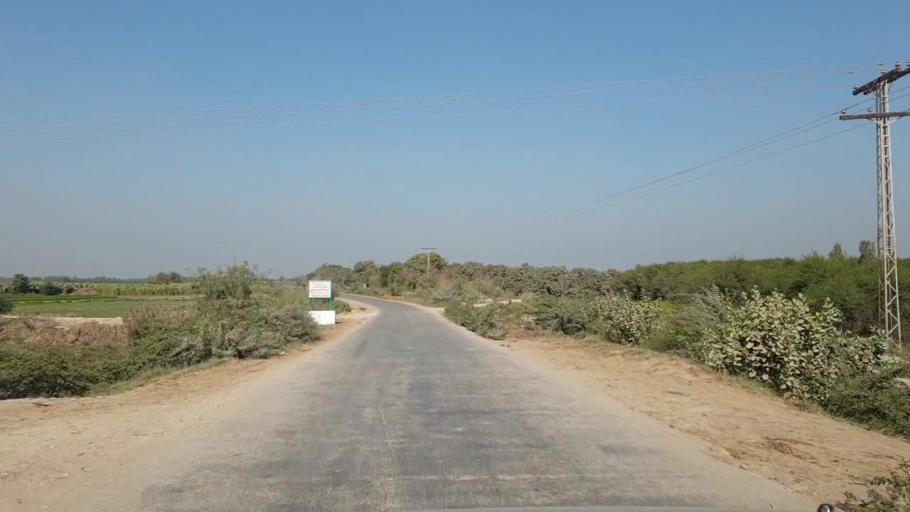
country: PK
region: Sindh
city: Tando Adam
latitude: 25.6501
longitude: 68.5898
